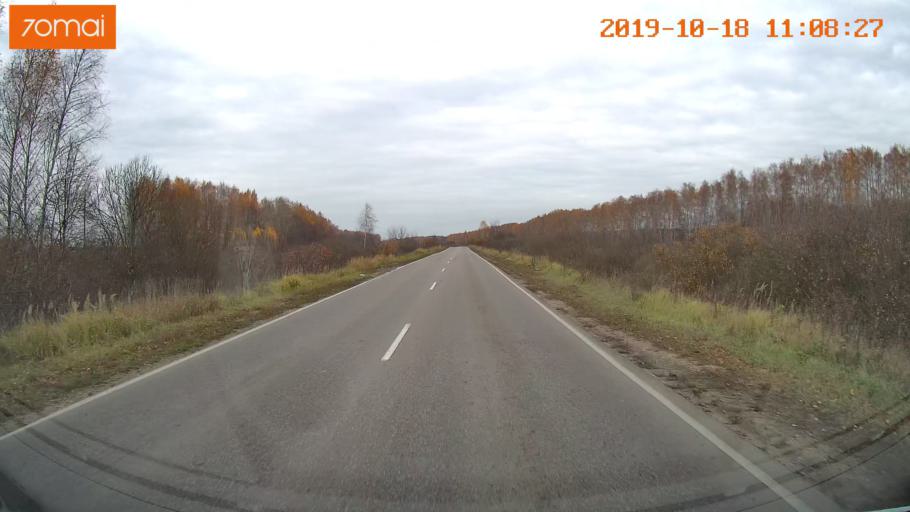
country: RU
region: Tula
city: Kimovsk
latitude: 53.9383
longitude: 38.5371
